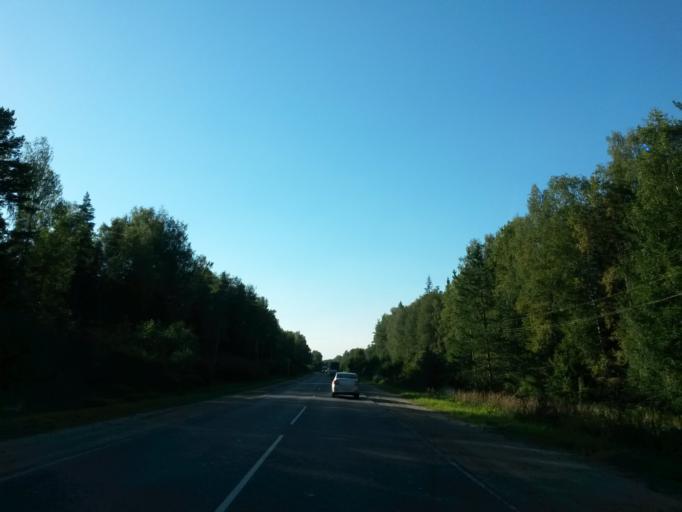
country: RU
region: Ivanovo
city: Novo-Talitsy
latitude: 57.0555
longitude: 40.7299
